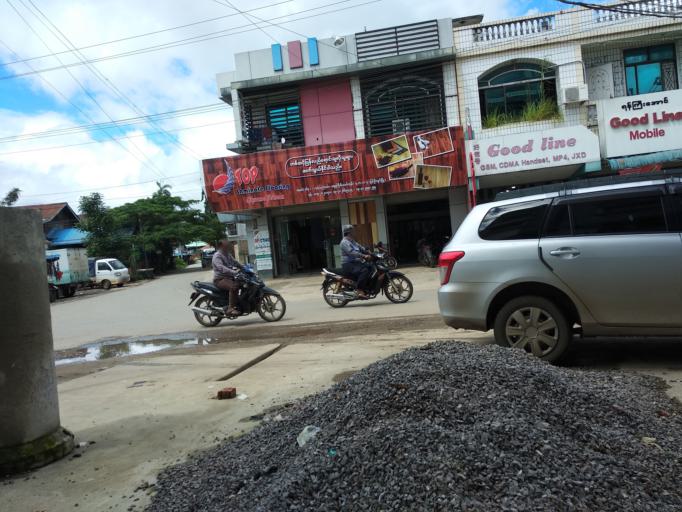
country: MM
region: Mandalay
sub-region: Pyin Oo Lwin District
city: Pyin Oo Lwin
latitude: 22.0253
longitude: 96.4676
